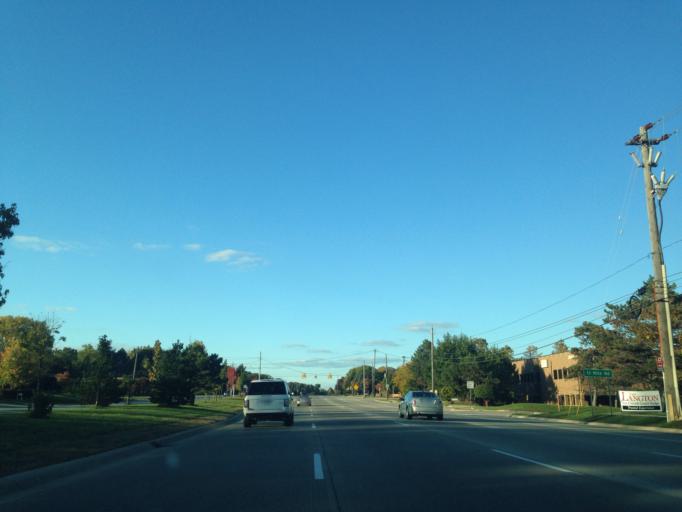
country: US
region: Michigan
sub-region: Oakland County
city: Bingham Farms
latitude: 42.5138
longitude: -83.2856
